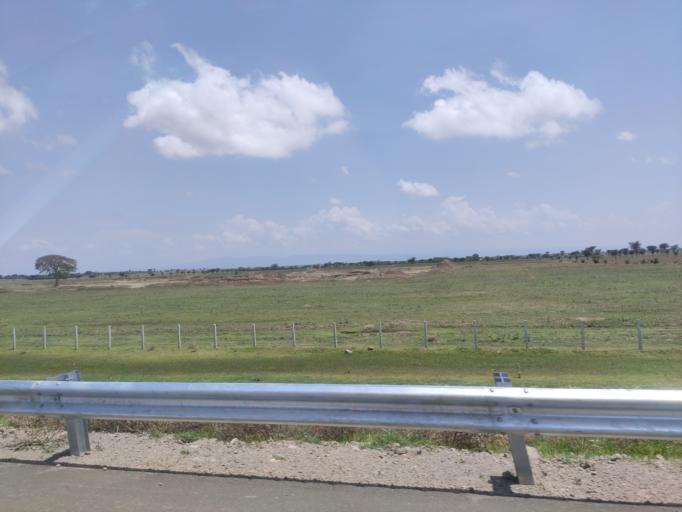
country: ET
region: Oromiya
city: Ziway
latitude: 8.2375
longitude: 38.8783
